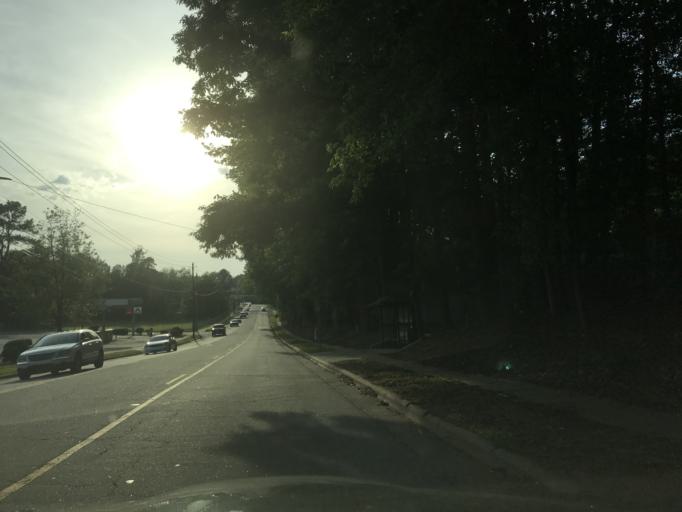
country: US
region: North Carolina
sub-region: Wake County
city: Raleigh
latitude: 35.7417
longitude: -78.6359
